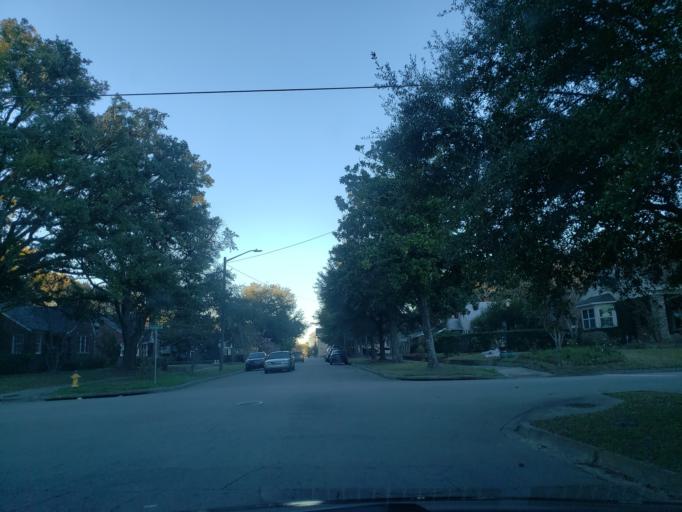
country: US
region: Georgia
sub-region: Chatham County
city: Thunderbolt
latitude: 32.0388
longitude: -81.0911
